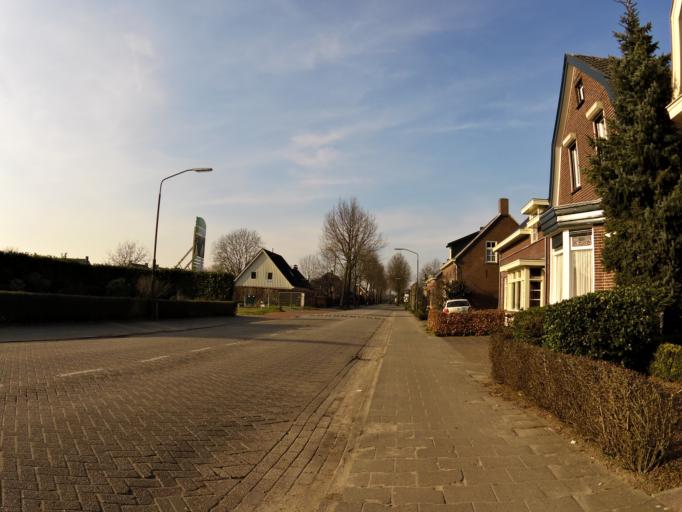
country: NL
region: North Brabant
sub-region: Gemeente Haaren
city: Haaren
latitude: 51.6369
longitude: 5.2321
